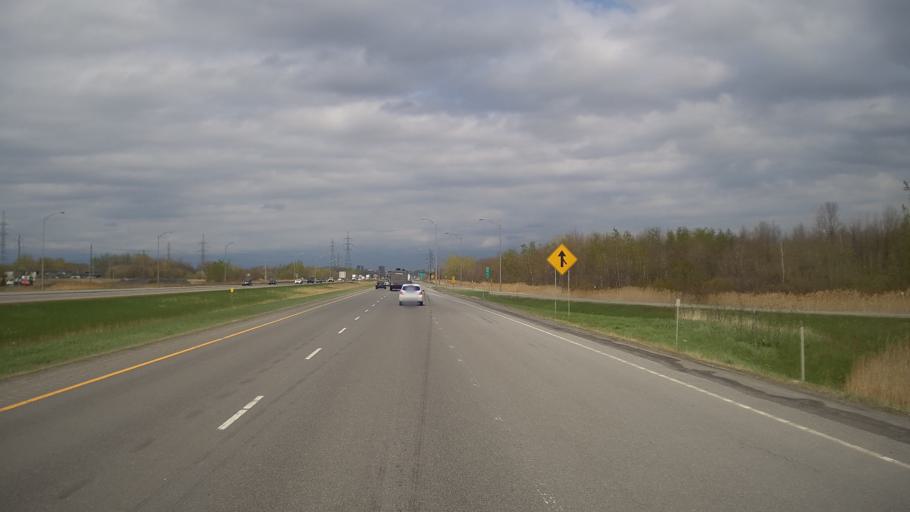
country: CA
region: Quebec
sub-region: Monteregie
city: La Prairie
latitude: 45.4047
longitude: -73.4602
